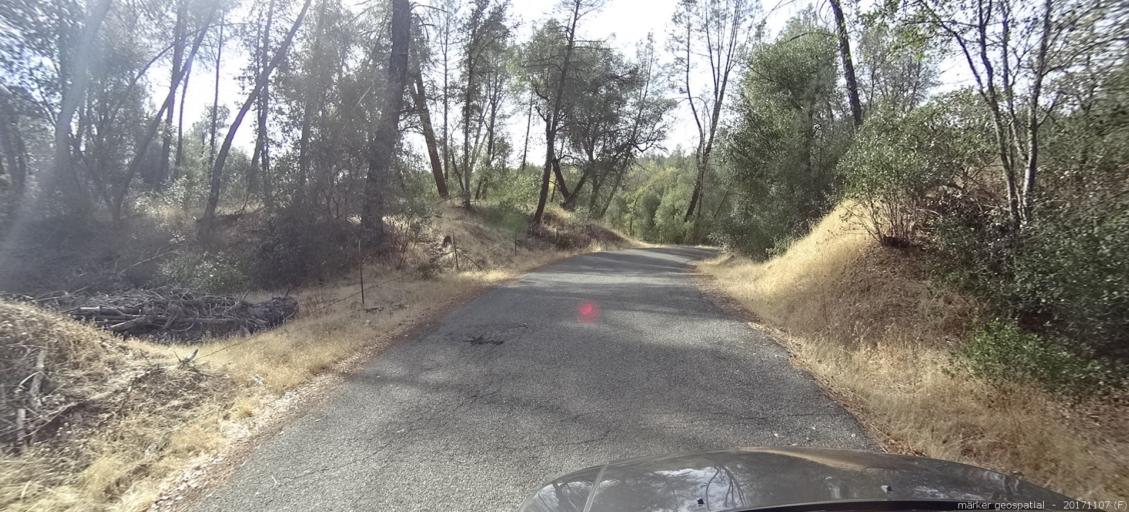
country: US
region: California
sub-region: Shasta County
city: Shasta
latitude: 40.4151
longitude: -122.5304
